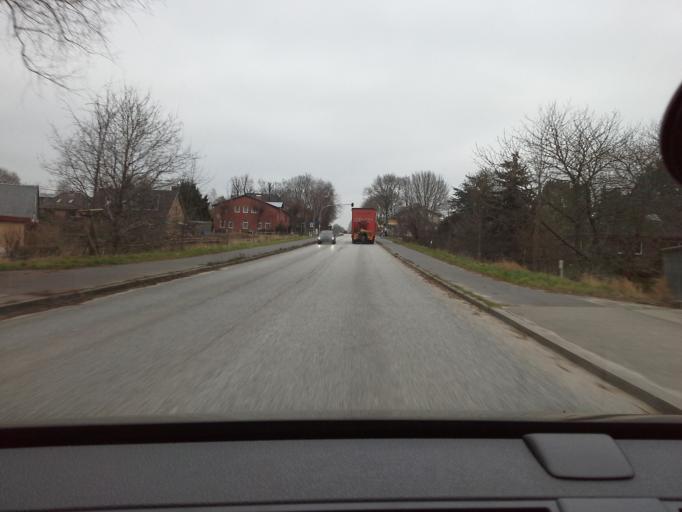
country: DE
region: Schleswig-Holstein
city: Lentfohrden
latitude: 53.8723
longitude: 9.8886
